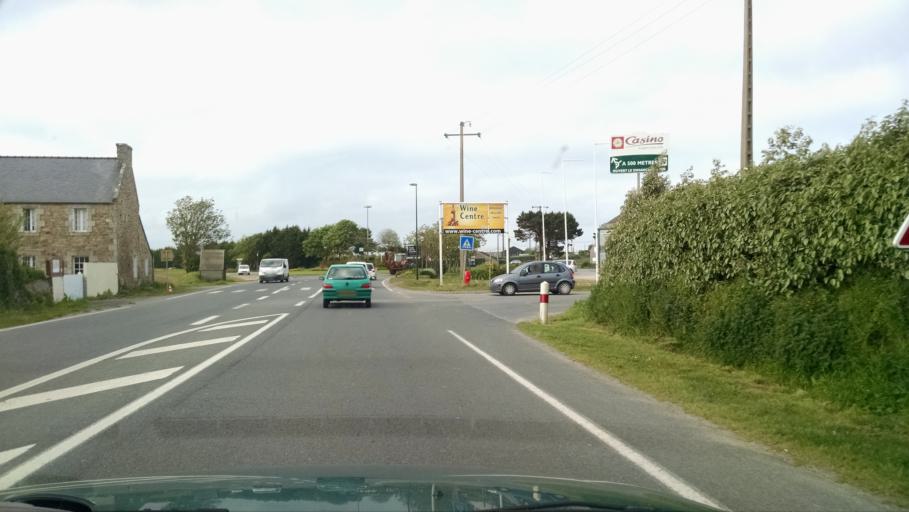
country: FR
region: Brittany
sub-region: Departement du Finistere
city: Roscoff
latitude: 48.7081
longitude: -3.9839
